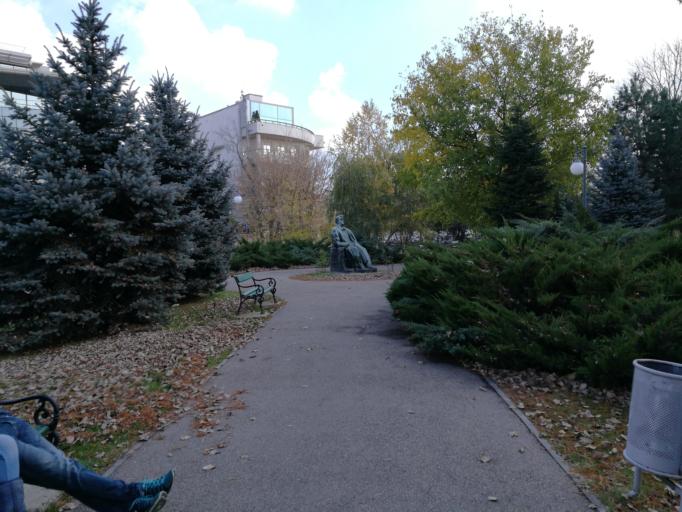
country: RO
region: Bucuresti
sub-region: Municipiul Bucuresti
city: Bucharest
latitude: 44.4766
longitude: 26.0885
